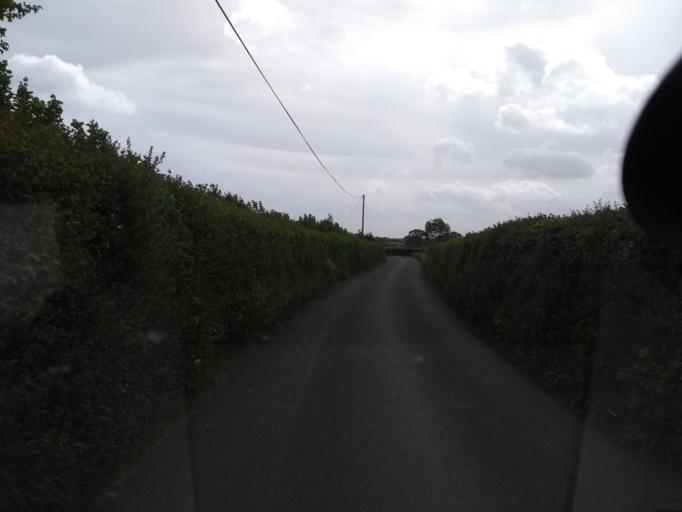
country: GB
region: England
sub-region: Somerset
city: Bishops Lydeard
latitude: 51.1757
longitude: -3.1868
